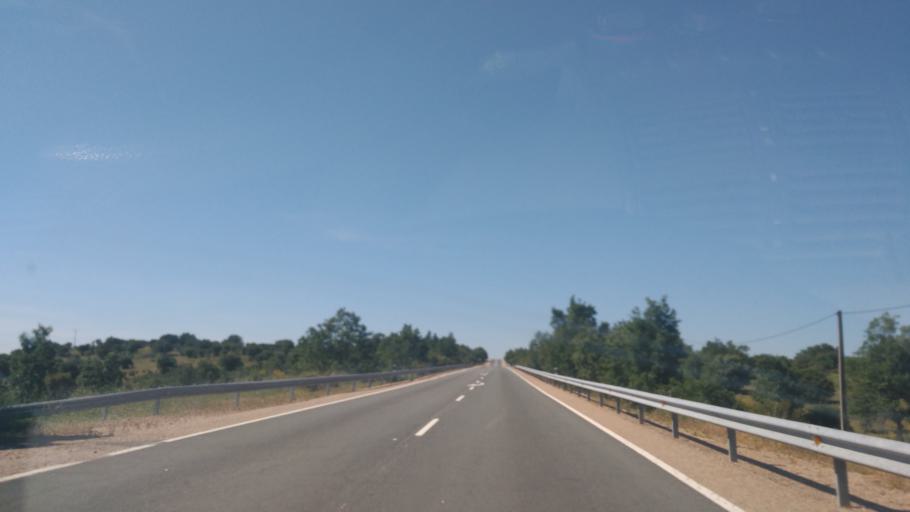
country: ES
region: Castille and Leon
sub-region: Provincia de Zamora
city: Cuelgamures
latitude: 41.2734
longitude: -5.7164
